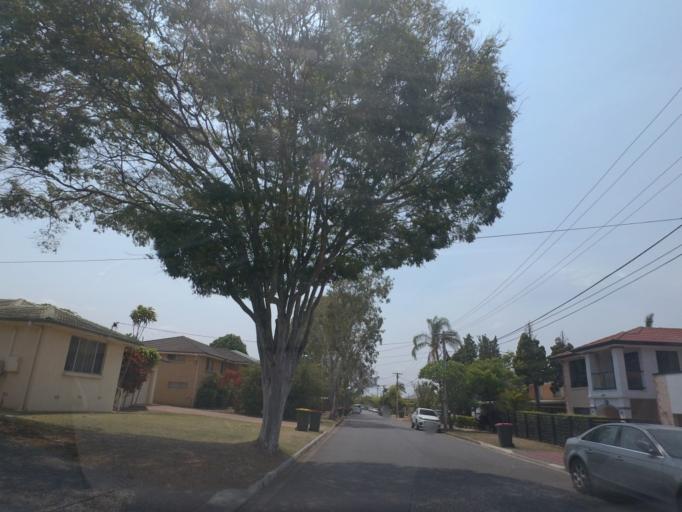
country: AU
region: Queensland
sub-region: Brisbane
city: Nathan
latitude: -27.5629
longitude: 153.0625
